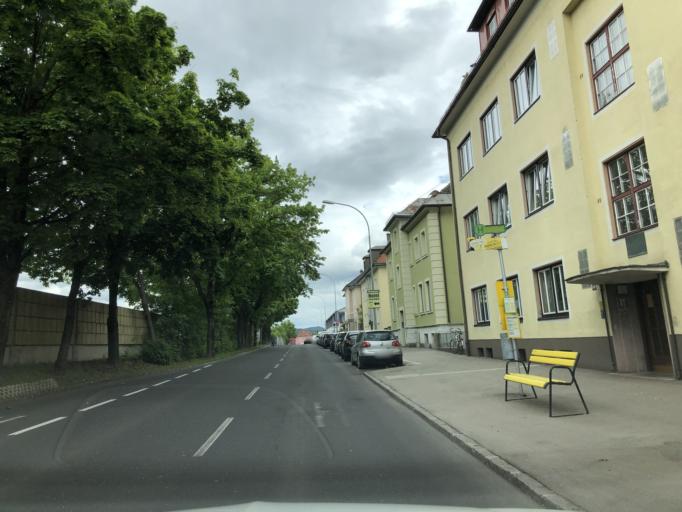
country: AT
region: Carinthia
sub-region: Villach Stadt
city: Villach
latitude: 46.6187
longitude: 13.8557
